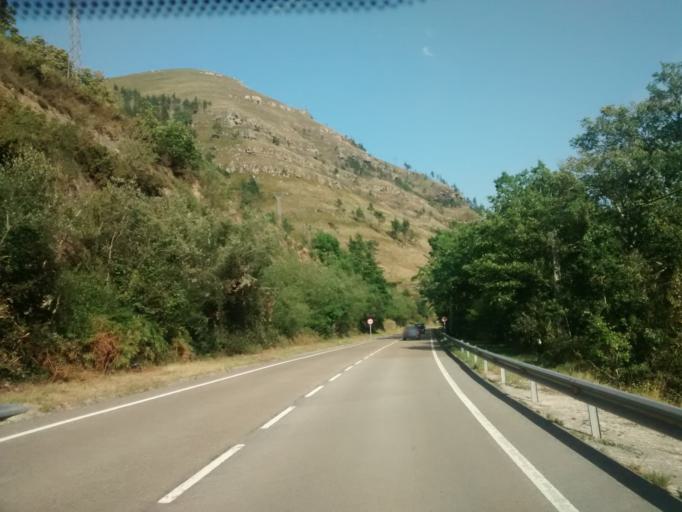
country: ES
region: Cantabria
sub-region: Provincia de Cantabria
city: Ruente
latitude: 43.1657
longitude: -4.2656
